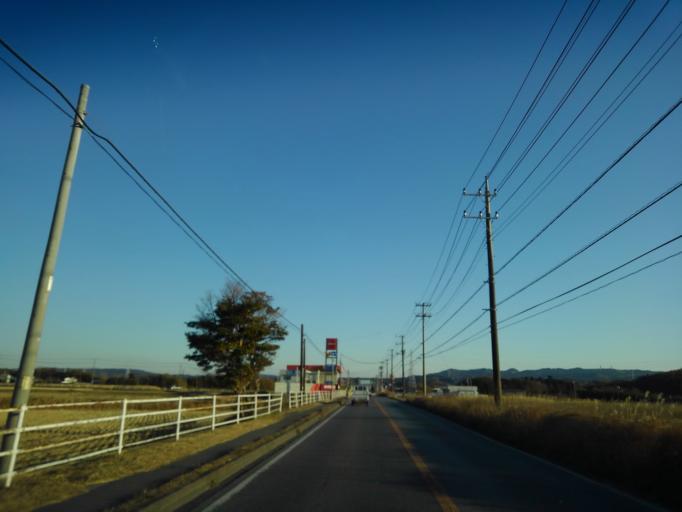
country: JP
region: Chiba
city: Kimitsu
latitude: 35.3155
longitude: 139.9325
